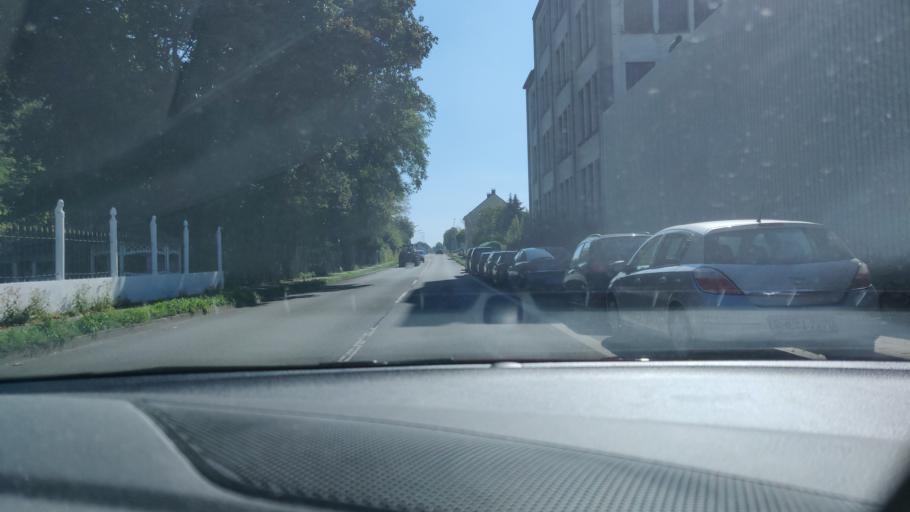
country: DE
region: North Rhine-Westphalia
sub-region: Regierungsbezirk Dusseldorf
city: Velbert
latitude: 51.3227
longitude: 7.0600
